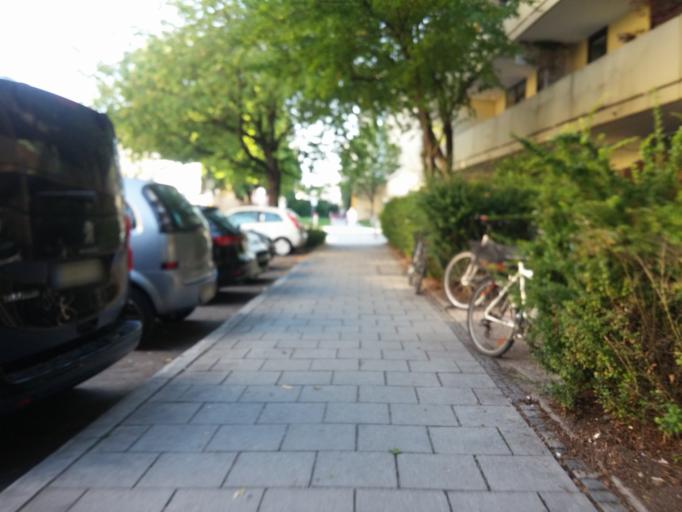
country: DE
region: Bavaria
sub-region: Upper Bavaria
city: Munich
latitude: 48.1126
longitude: 11.5371
